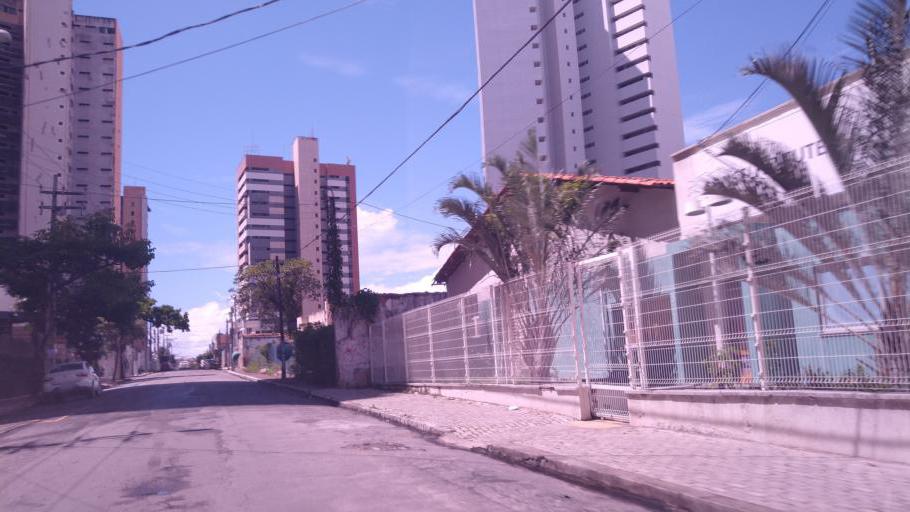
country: BR
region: Ceara
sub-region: Fortaleza
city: Fortaleza
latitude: -3.7249
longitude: -38.4871
